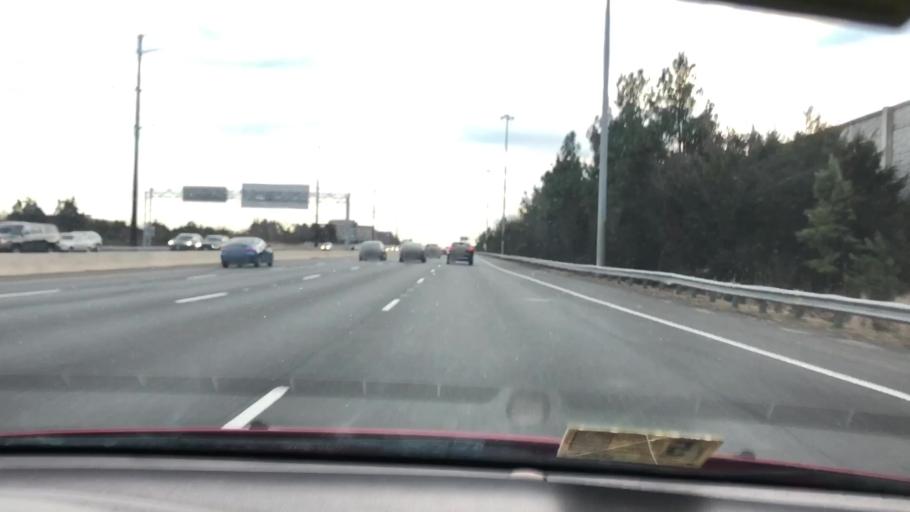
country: US
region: Virginia
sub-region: Fairfax County
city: Floris
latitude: 38.9448
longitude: -77.4299
